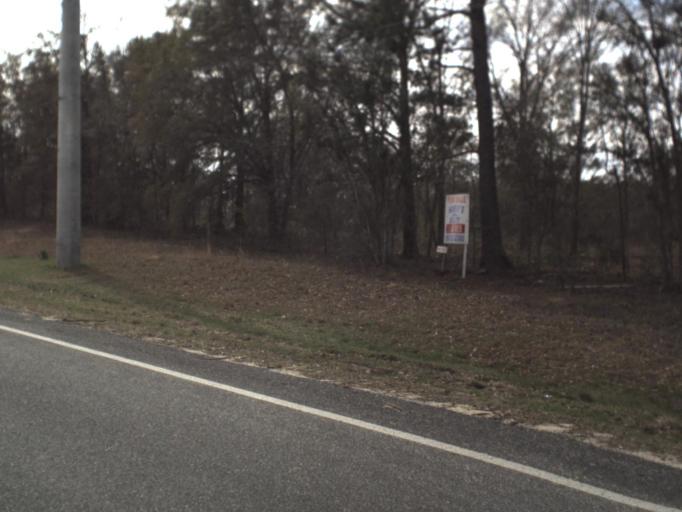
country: US
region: Florida
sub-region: Washington County
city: Chipley
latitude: 30.7329
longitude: -85.3867
